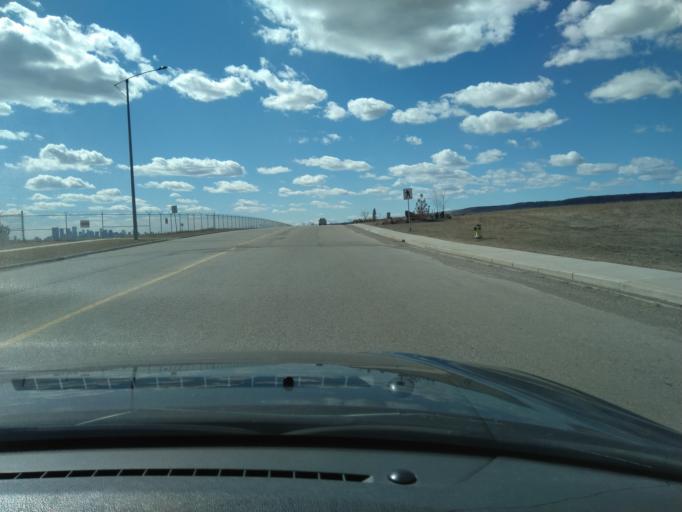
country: CA
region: Alberta
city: Calgary
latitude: 51.1311
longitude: -114.0383
